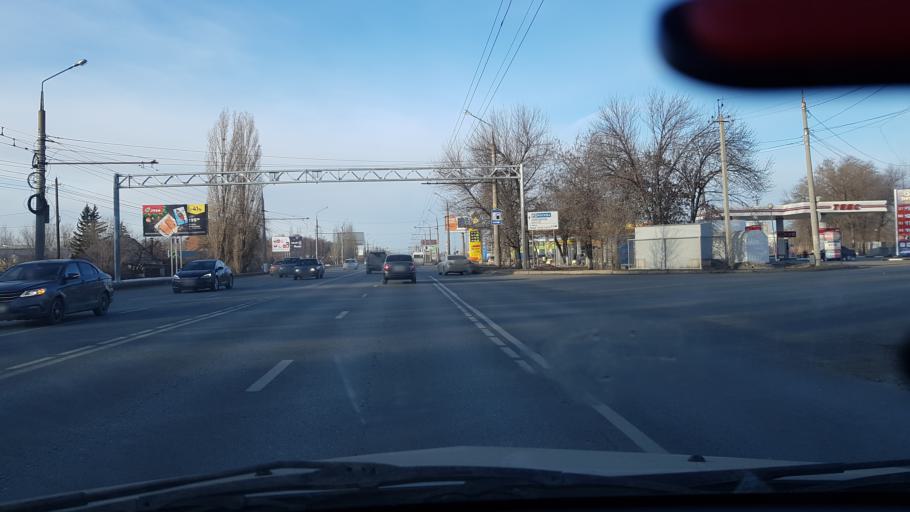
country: RU
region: Samara
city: Tol'yatti
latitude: 53.5365
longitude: 49.3932
